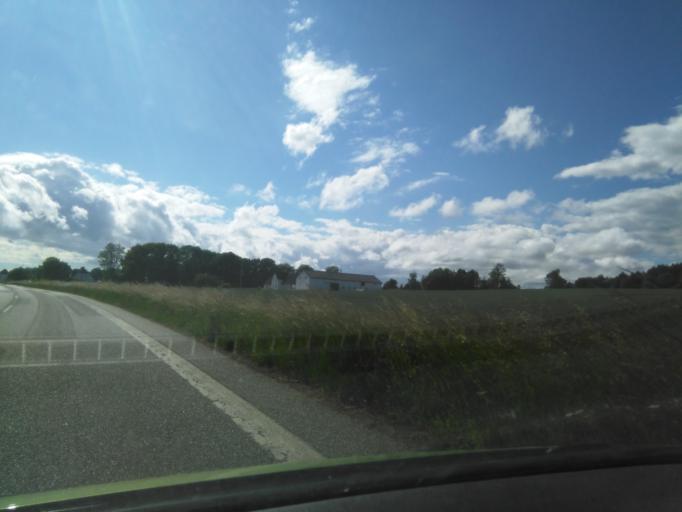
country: DK
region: Capital Region
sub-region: Bornholm Kommune
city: Nexo
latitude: 55.0633
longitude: 15.0832
